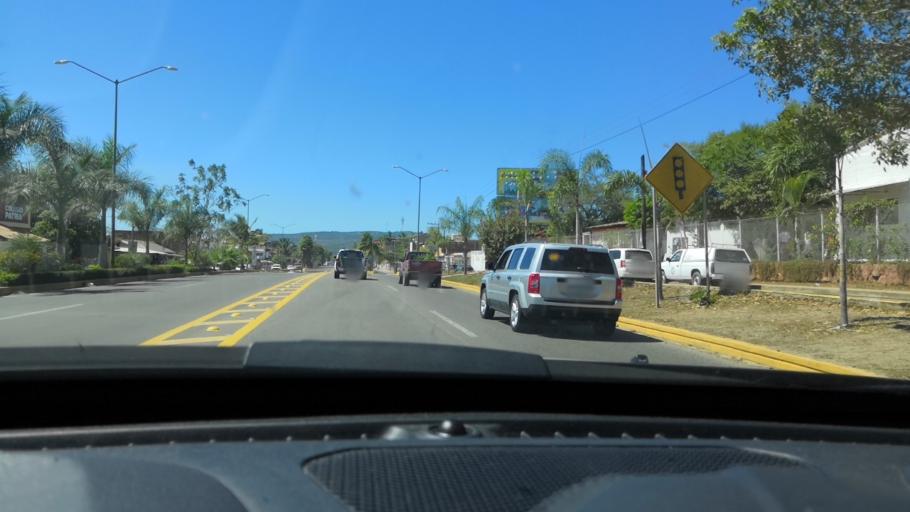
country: MX
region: Nayarit
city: Las Varas
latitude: 21.1818
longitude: -105.1328
